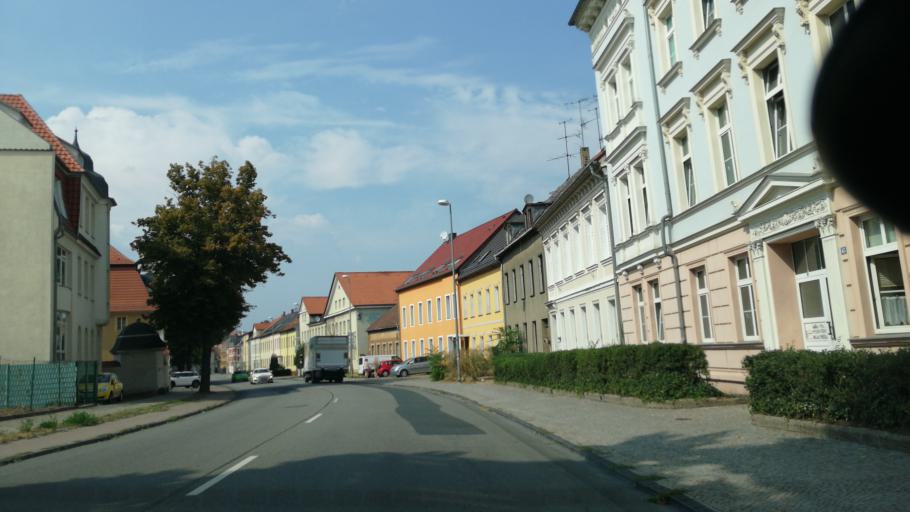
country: DE
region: Saxony-Anhalt
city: Volkstedt
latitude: 51.5251
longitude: 11.5544
